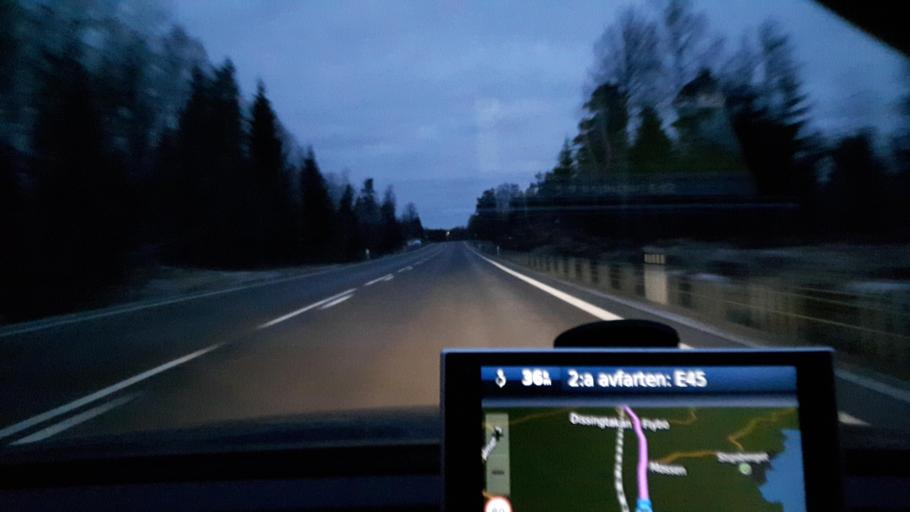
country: SE
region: Vaestra Goetaland
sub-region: Vanersborgs Kommun
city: Vanersborg
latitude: 58.4129
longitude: 12.2930
